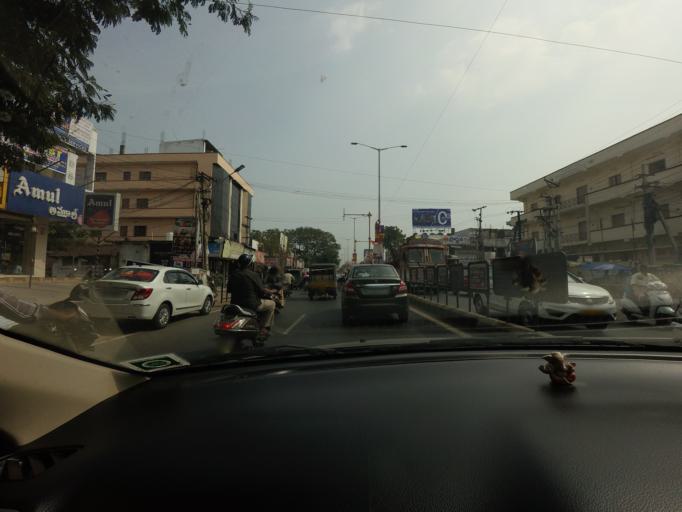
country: IN
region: Andhra Pradesh
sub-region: Krishna
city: Yanamalakuduru
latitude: 16.4955
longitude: 80.6604
